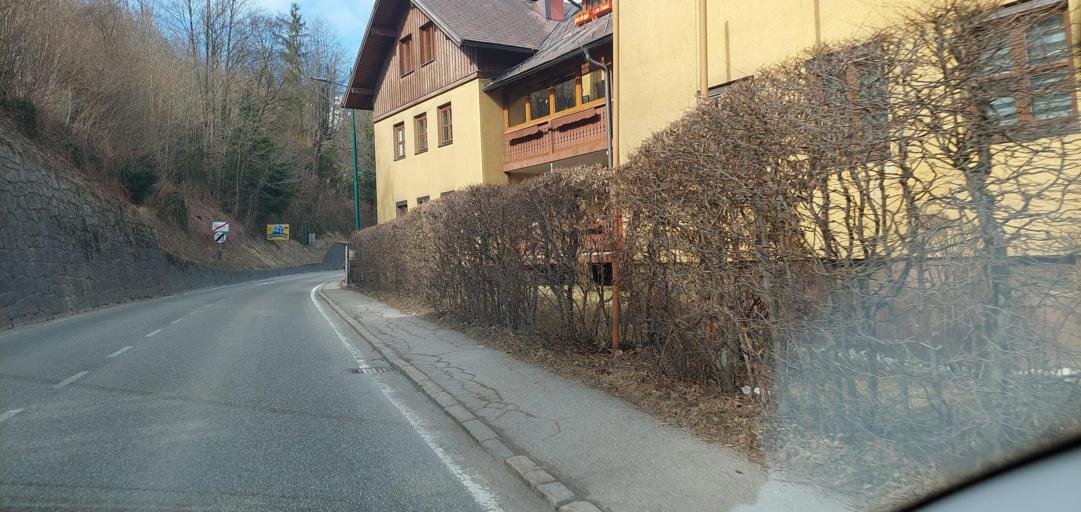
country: AT
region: Upper Austria
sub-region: Politischer Bezirk Gmunden
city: Bad Ischl
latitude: 47.7148
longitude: 13.6150
